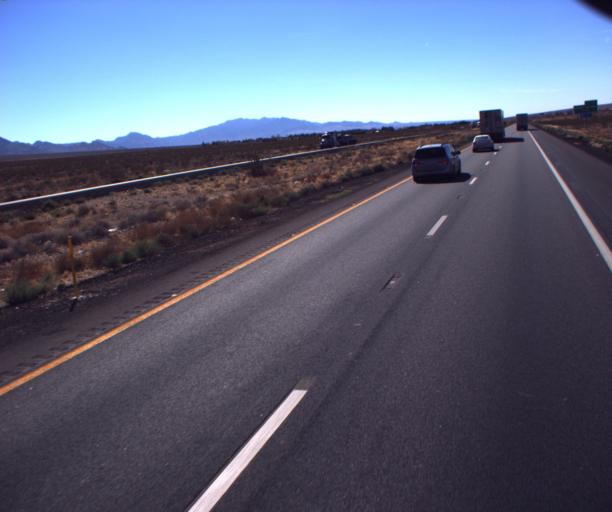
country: US
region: Arizona
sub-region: Mohave County
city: Beaver Dam
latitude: 36.9094
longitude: -113.8879
